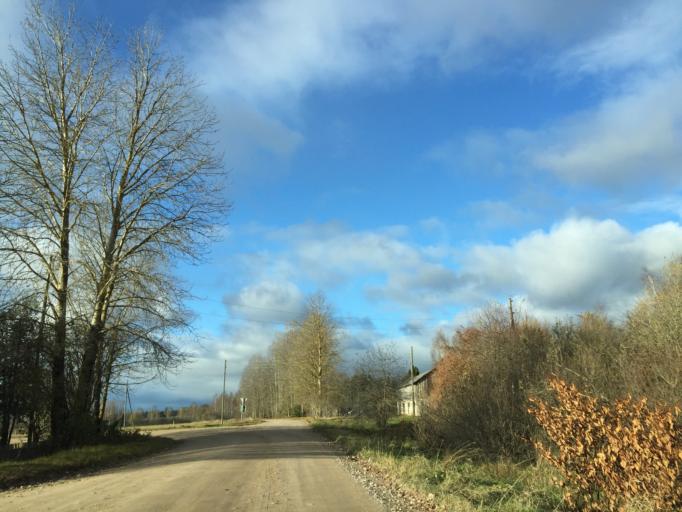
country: LV
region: Tukuma Rajons
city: Tukums
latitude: 56.9814
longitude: 22.9902
